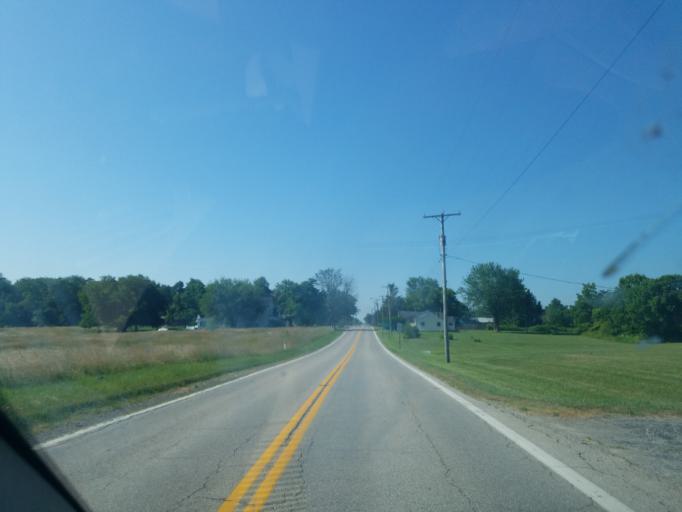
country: US
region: Ohio
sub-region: Union County
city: Richwood
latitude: 40.4104
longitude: -83.4531
